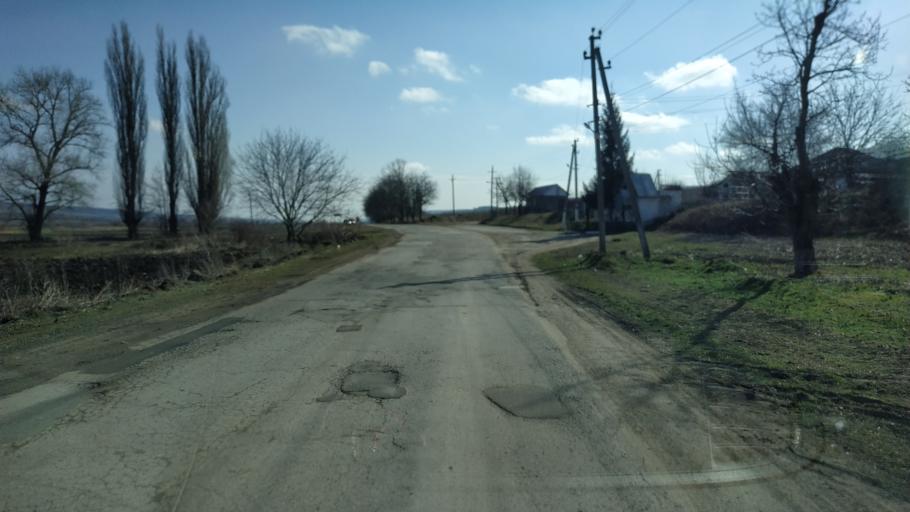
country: MD
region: Hincesti
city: Hincesti
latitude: 46.9516
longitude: 28.6116
